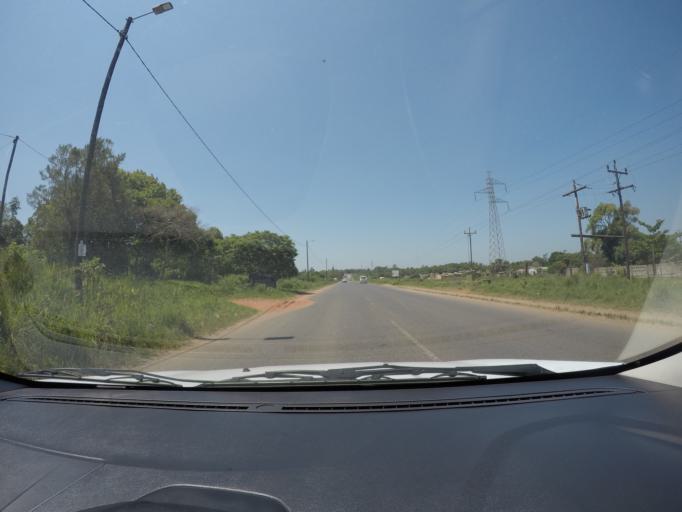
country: ZA
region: KwaZulu-Natal
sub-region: uThungulu District Municipality
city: eSikhawini
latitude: -28.8319
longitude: 31.9406
